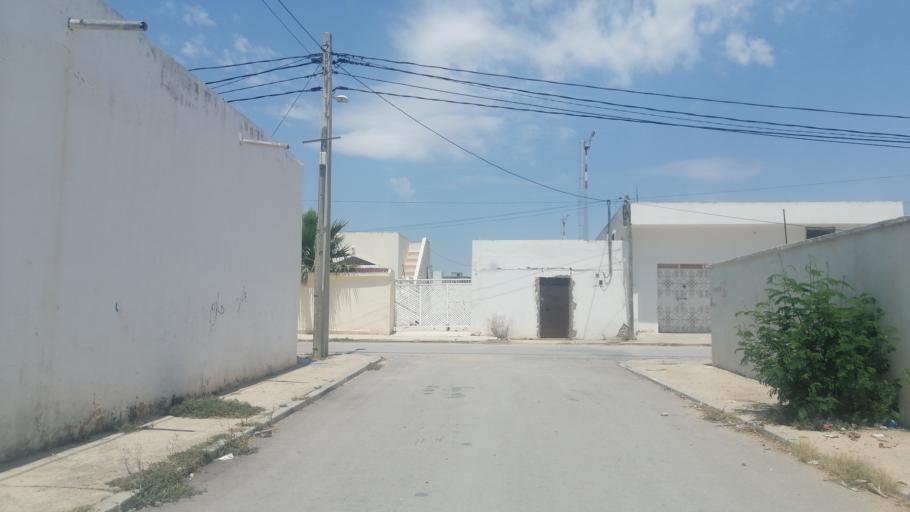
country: TN
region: Al Qayrawan
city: Sbikha
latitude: 36.1202
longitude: 10.0915
